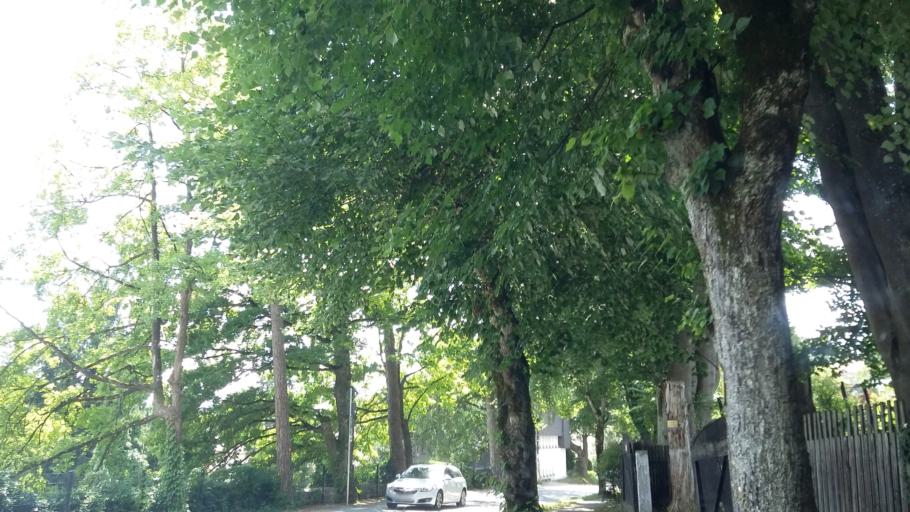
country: DE
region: Bavaria
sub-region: Upper Bavaria
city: Starnberg
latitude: 48.0050
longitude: 11.3406
